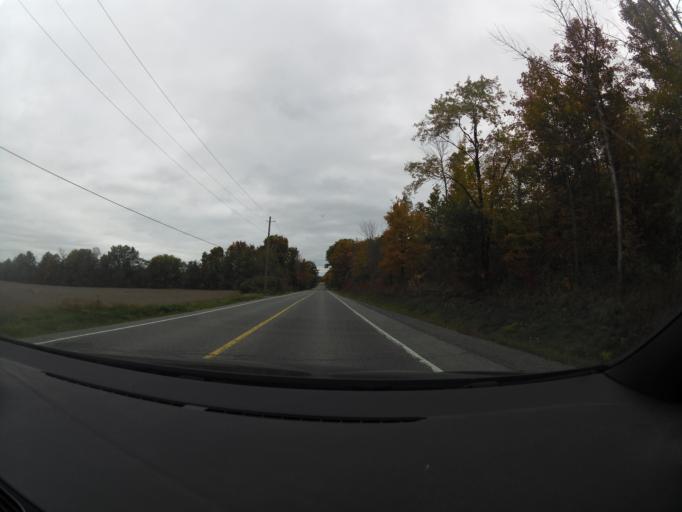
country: CA
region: Ontario
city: Bells Corners
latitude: 45.3375
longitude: -75.9811
